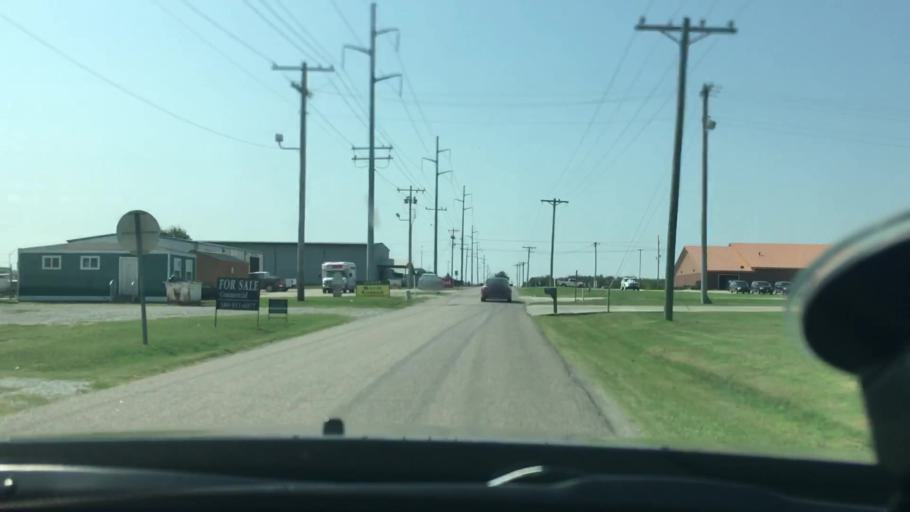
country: US
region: Oklahoma
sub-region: Bryan County
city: Durant
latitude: 33.9999
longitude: -96.4253
